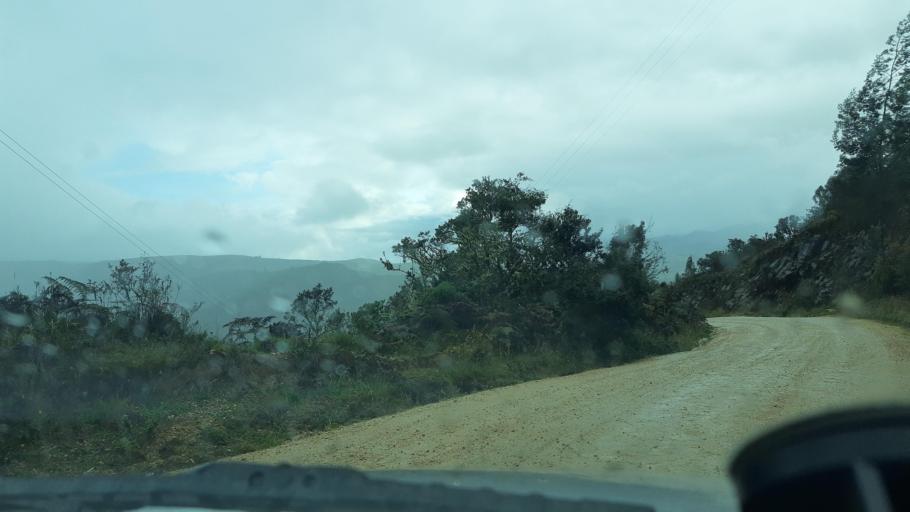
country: CO
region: Cundinamarca
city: Villapinzon
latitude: 5.2082
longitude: -73.5719
